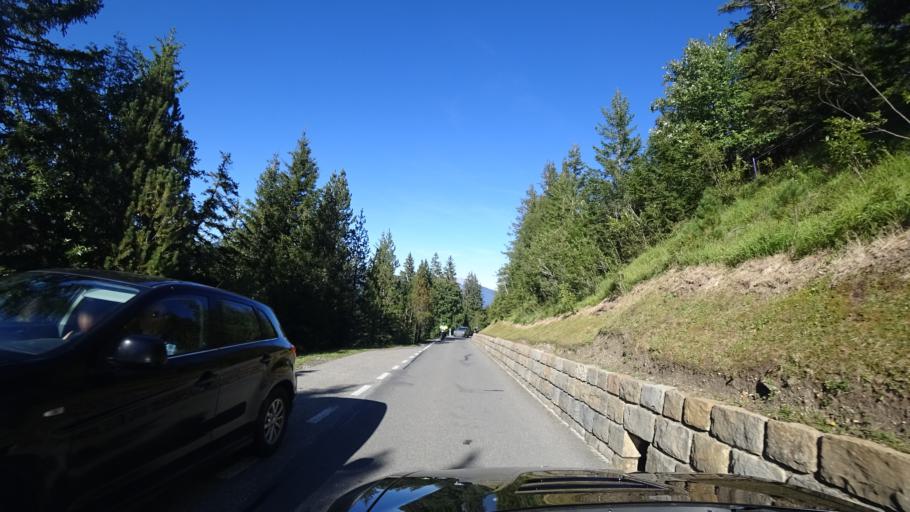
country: CH
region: Obwalden
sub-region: Obwalden
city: Lungern
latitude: 46.8230
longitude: 8.0974
